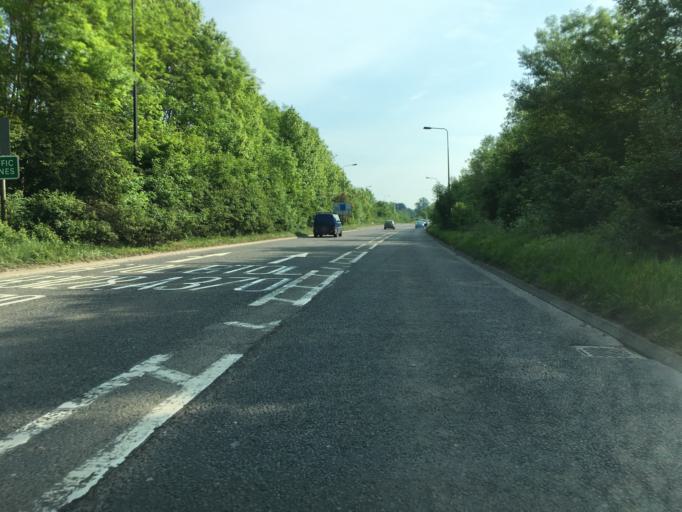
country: GB
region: England
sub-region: North Somerset
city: Long Ashton
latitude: 51.4350
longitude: -2.6403
